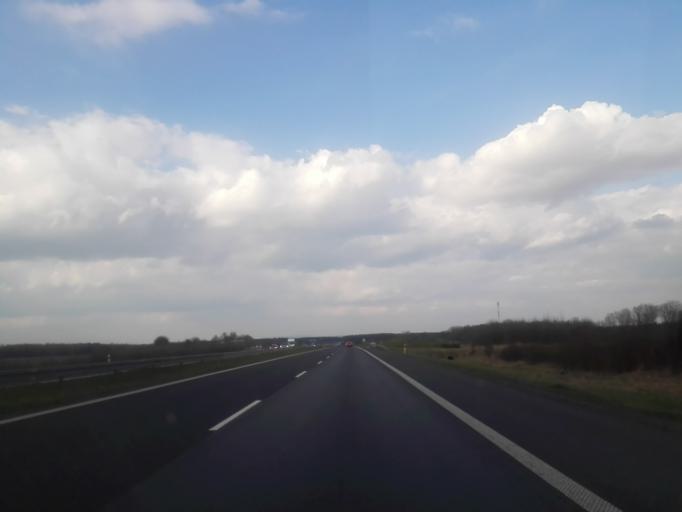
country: PL
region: Silesian Voivodeship
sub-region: Powiat czestochowski
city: Borowno
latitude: 50.9868
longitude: 19.2831
